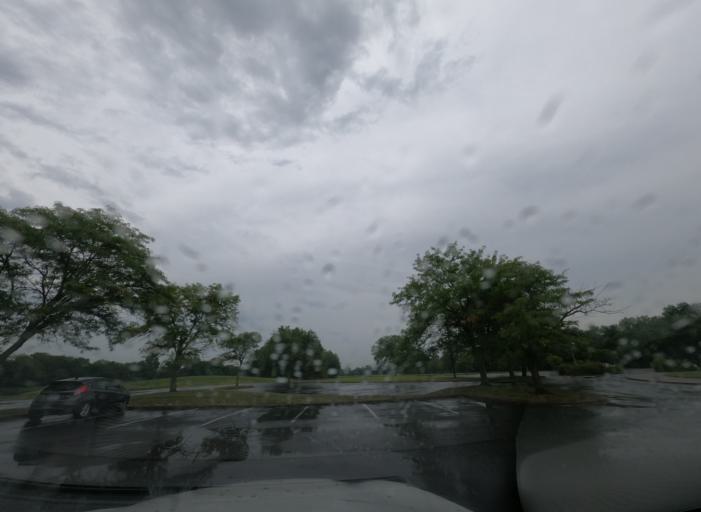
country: US
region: Illinois
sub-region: Saint Clair County
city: Fairmont City
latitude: 38.6540
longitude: -90.0588
